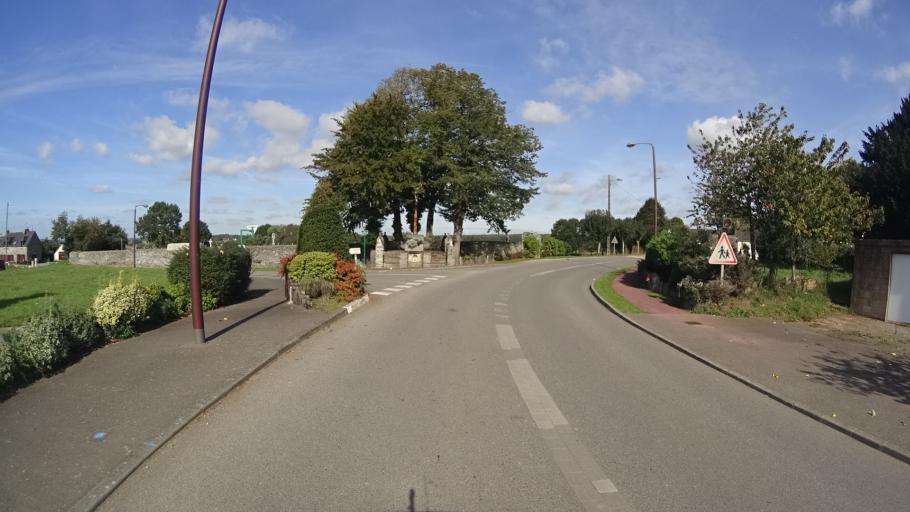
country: FR
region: Brittany
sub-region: Departement du Morbihan
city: Peillac
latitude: 47.7410
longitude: -2.2139
